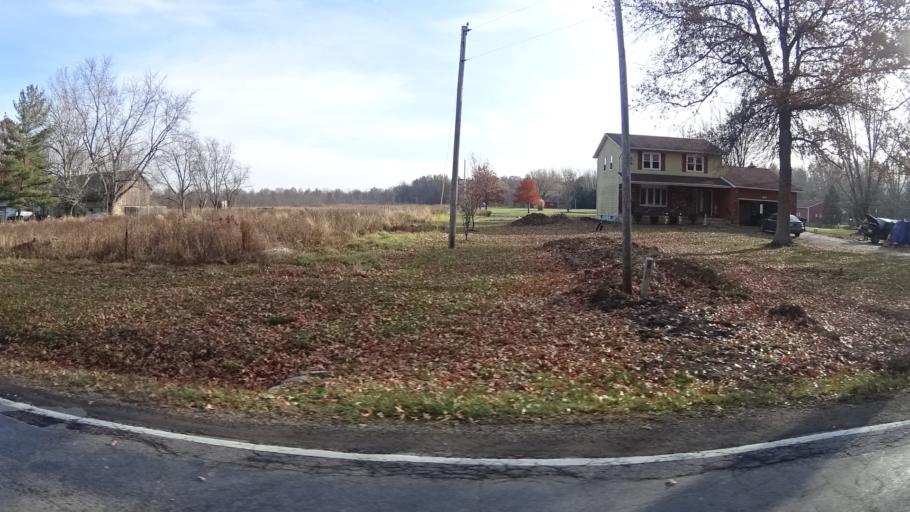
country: US
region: Ohio
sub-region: Lorain County
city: Eaton Estates
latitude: 41.2707
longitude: -81.9824
